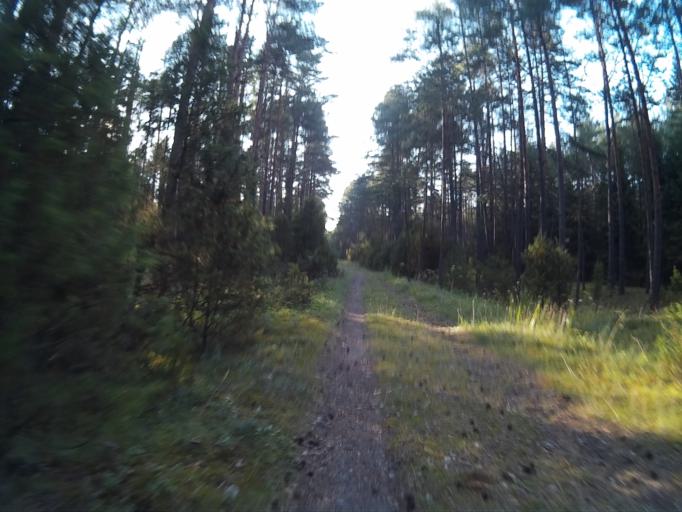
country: PL
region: Kujawsko-Pomorskie
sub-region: Powiat tucholski
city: Cekcyn
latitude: 53.5520
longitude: 18.1042
